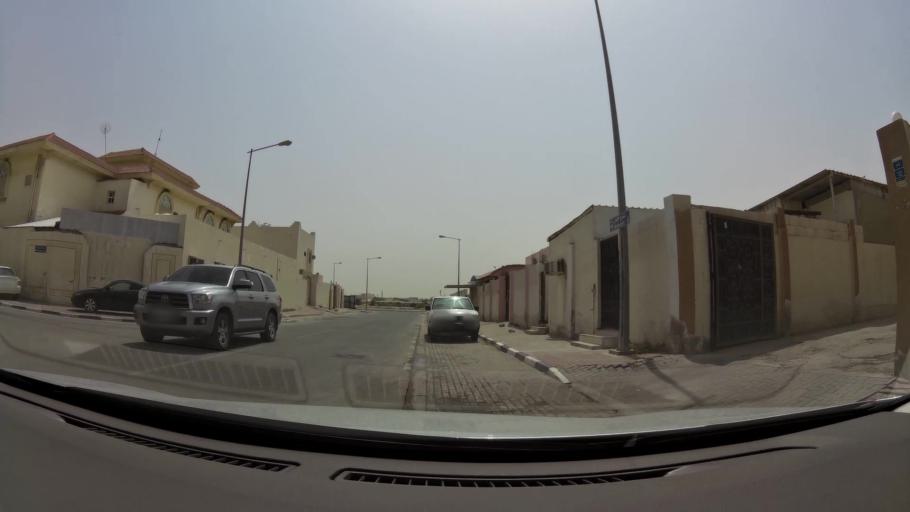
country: QA
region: Baladiyat ar Rayyan
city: Ar Rayyan
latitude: 25.2422
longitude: 51.4285
